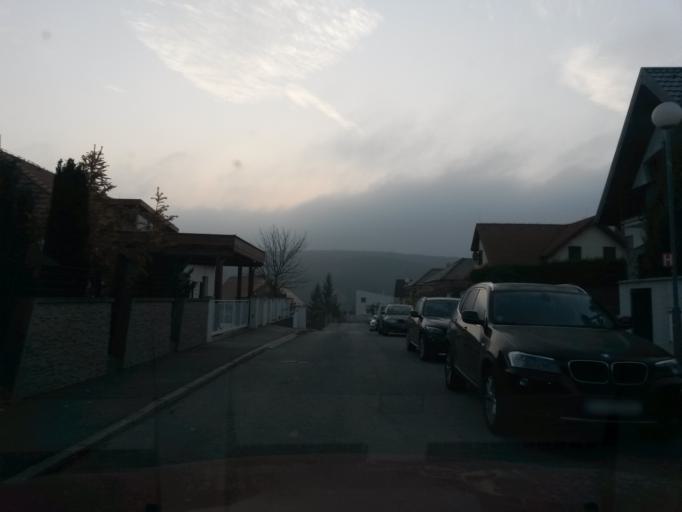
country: SK
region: Kosicky
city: Kosice
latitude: 48.7155
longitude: 21.2027
